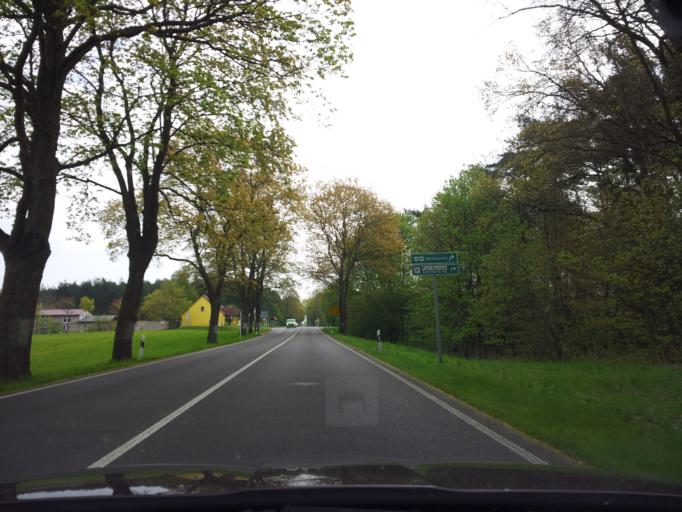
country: DE
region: Brandenburg
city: Lietzen
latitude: 52.5093
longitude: 14.2721
